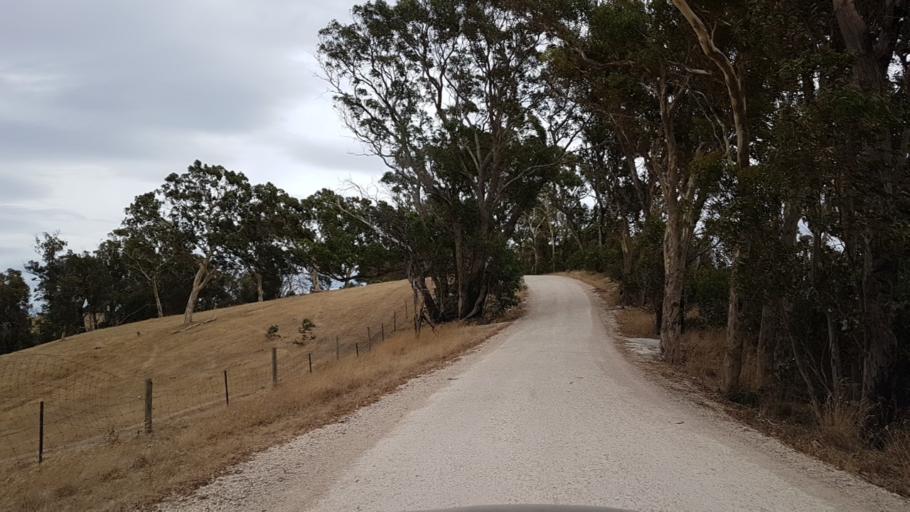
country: AU
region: South Australia
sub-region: Adelaide Hills
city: Gumeracha
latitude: -34.7962
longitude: 138.8167
